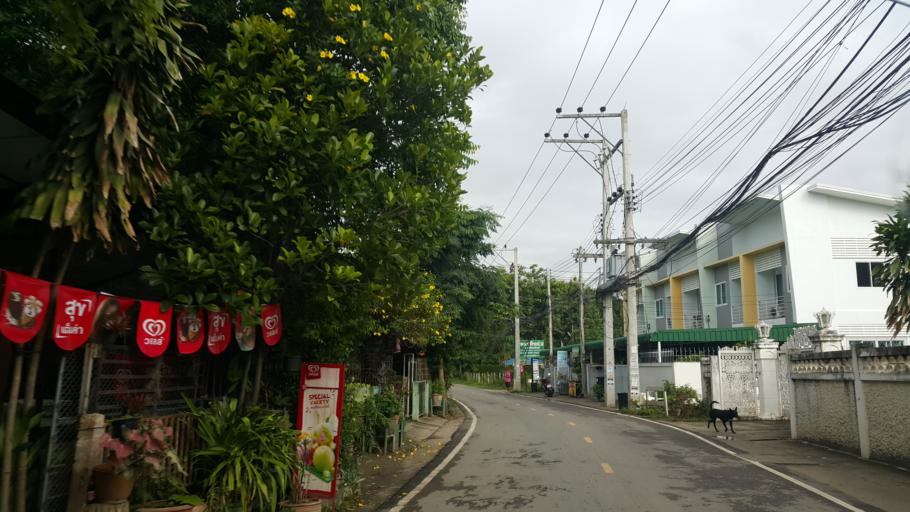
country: TH
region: Chiang Mai
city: Chiang Mai
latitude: 18.7478
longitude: 98.9698
